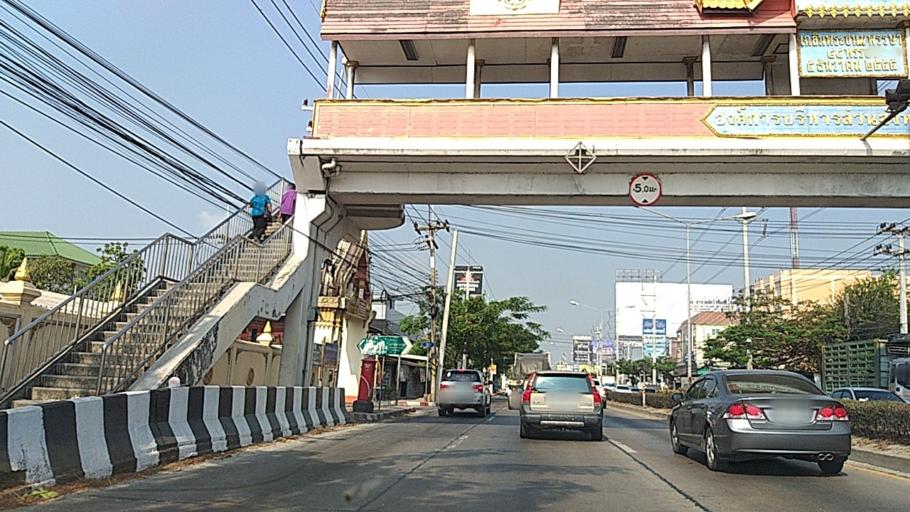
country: TH
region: Bangkok
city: Sai Mai
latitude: 13.9329
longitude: 100.6893
